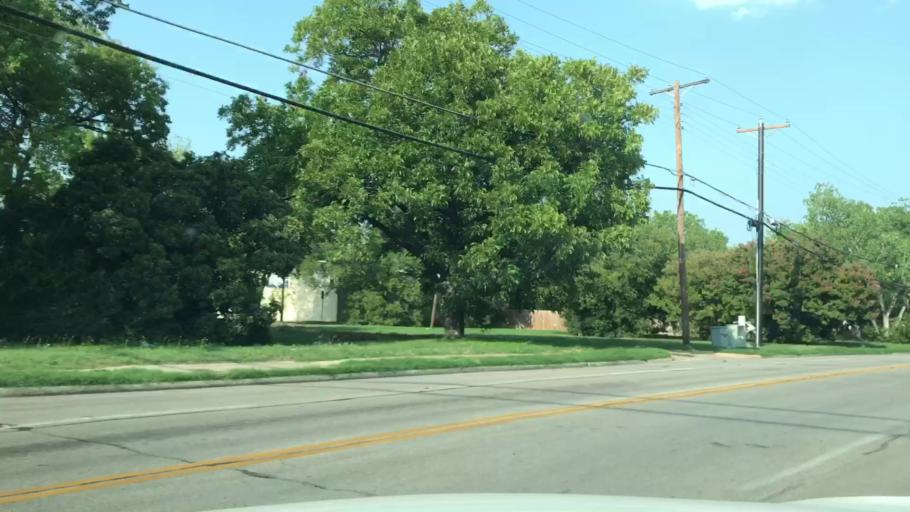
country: US
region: Texas
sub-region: Dallas County
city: Irving
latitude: 32.8221
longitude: -96.9423
